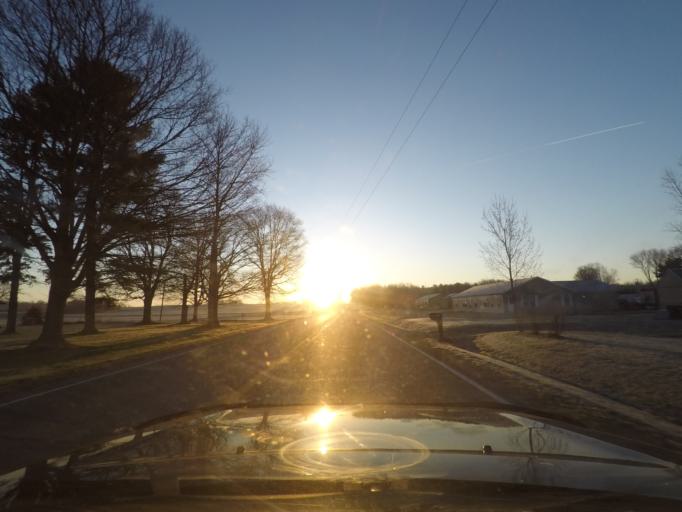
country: US
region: Indiana
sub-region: Saint Joseph County
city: North Liberty
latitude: 41.4485
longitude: -86.3700
